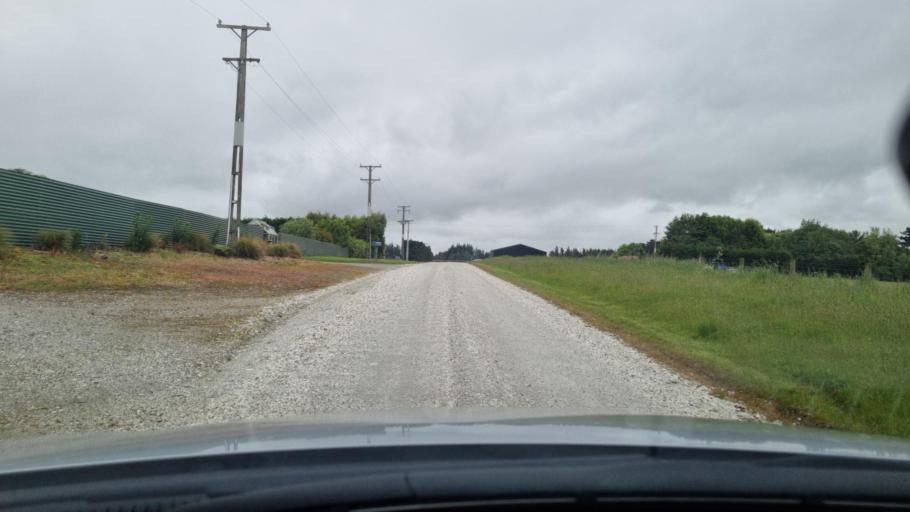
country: NZ
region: Southland
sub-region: Invercargill City
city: Invercargill
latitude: -46.4337
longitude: 168.4100
